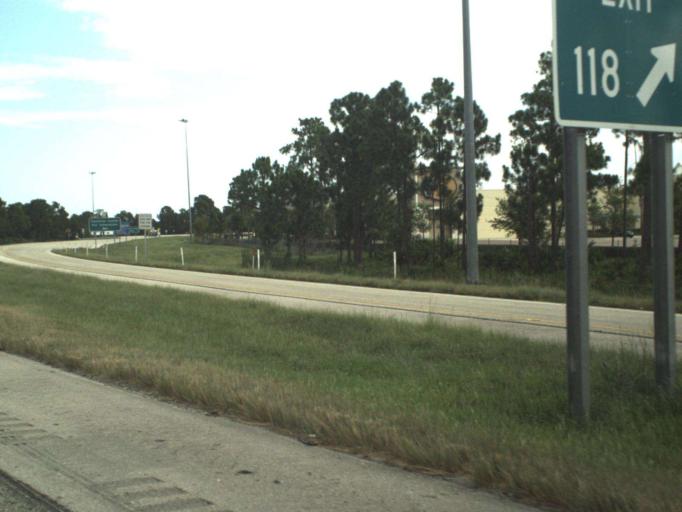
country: US
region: Florida
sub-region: Saint Lucie County
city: Port Saint Lucie
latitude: 27.2599
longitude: -80.4202
